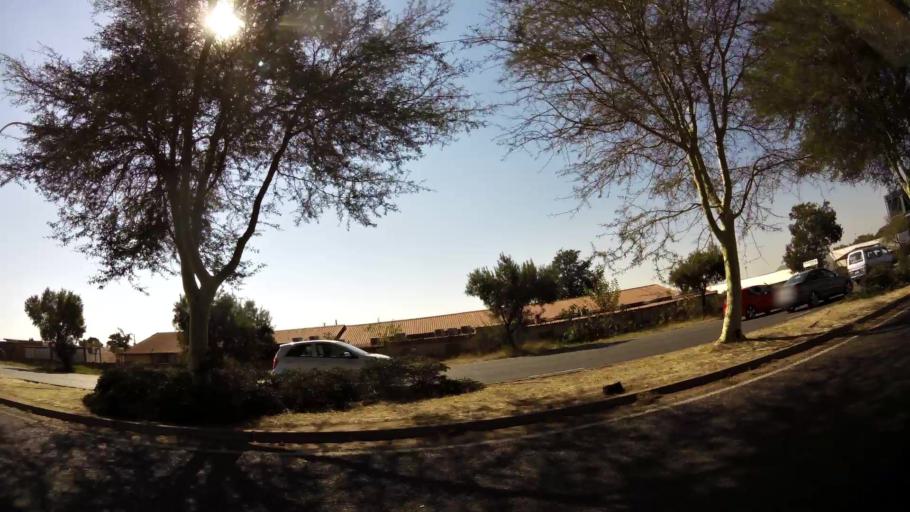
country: ZA
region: Gauteng
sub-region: City of Tshwane Metropolitan Municipality
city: Mabopane
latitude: -25.5264
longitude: 28.1082
